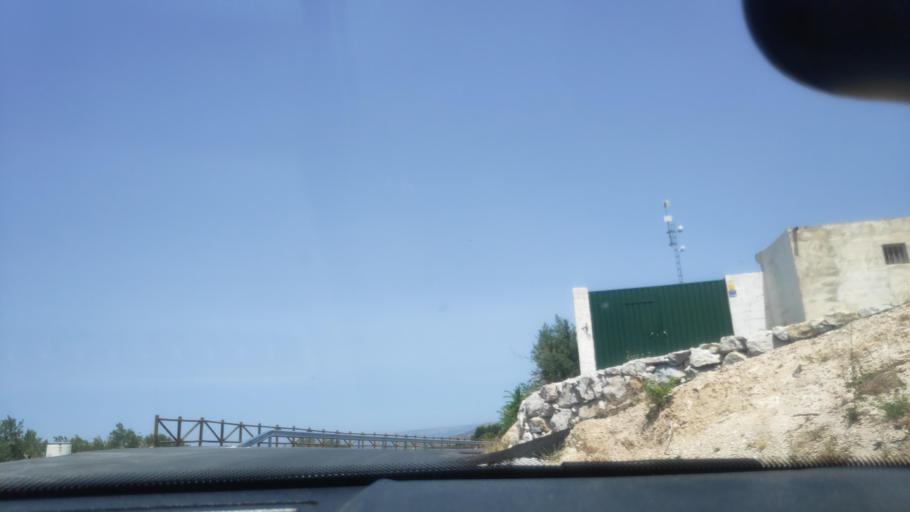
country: ES
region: Andalusia
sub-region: Provincia de Jaen
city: Jodar
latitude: 37.8135
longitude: -3.4134
